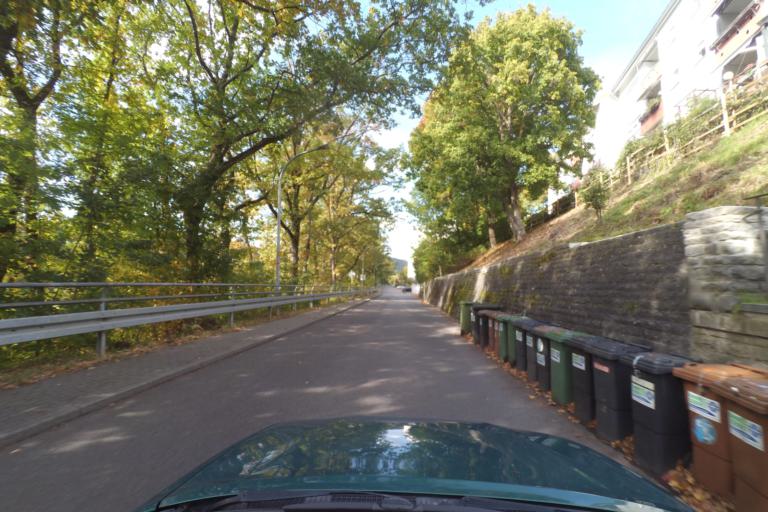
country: DE
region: Baden-Wuerttemberg
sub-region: Karlsruhe Region
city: Nagold
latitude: 48.5646
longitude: 8.7257
